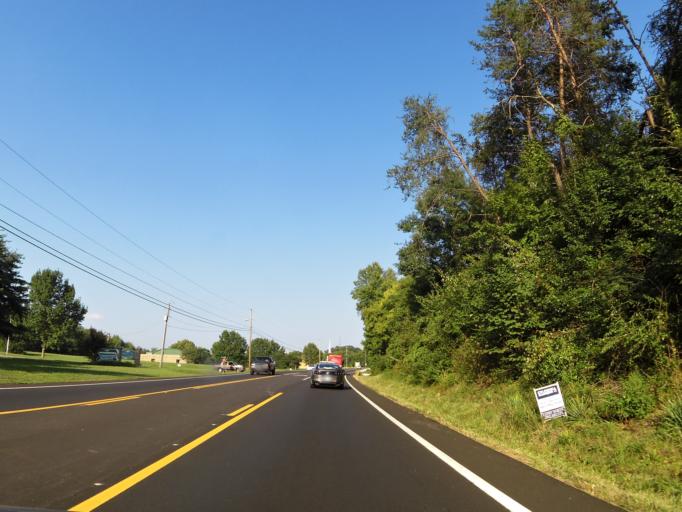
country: US
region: Tennessee
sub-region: Knox County
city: Knoxville
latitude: 35.8873
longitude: -83.9439
